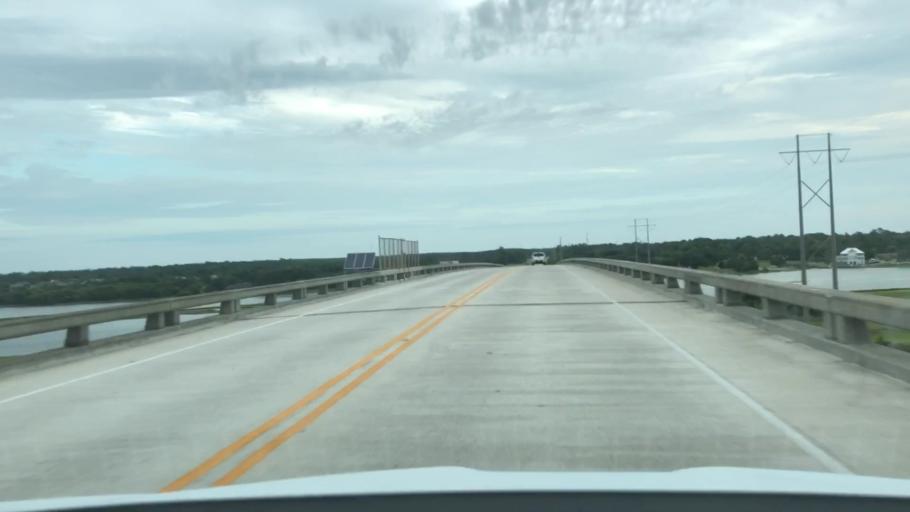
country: US
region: North Carolina
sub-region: Carteret County
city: Cedar Point
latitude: 34.6739
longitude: -77.0653
